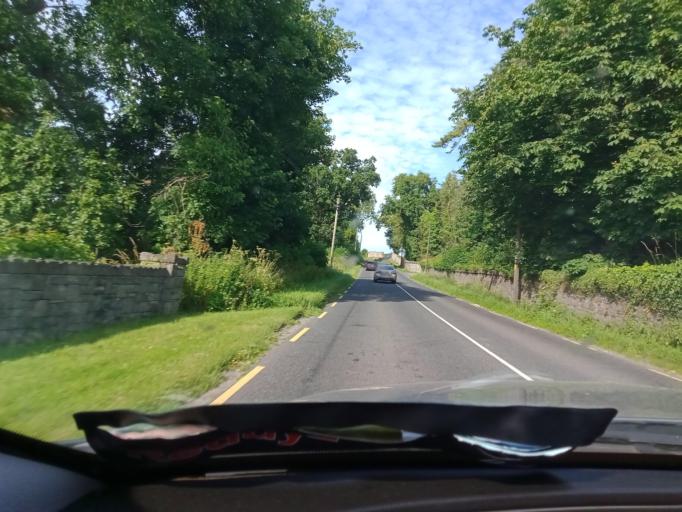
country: IE
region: Leinster
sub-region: An Iarmhi
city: An Muileann gCearr
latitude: 53.5780
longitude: -7.3150
